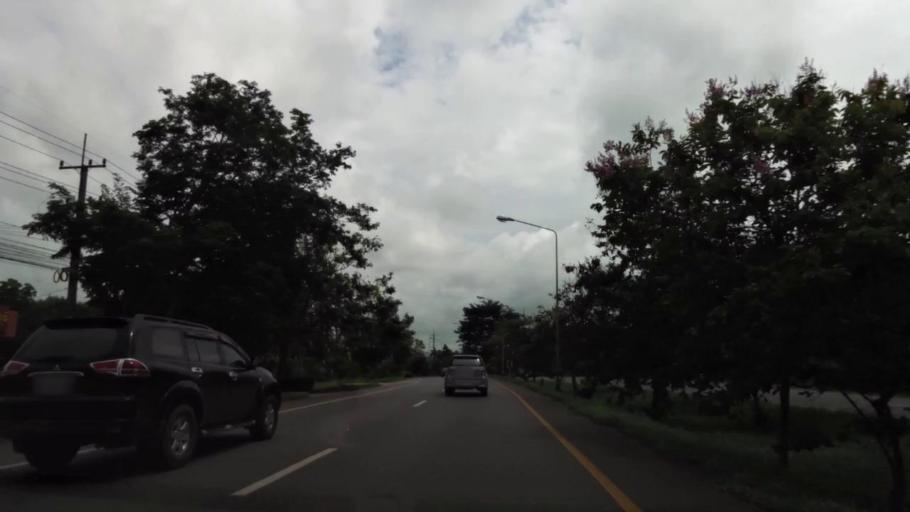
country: TH
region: Chanthaburi
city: Na Yai Am
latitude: 12.7417
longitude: 101.8903
